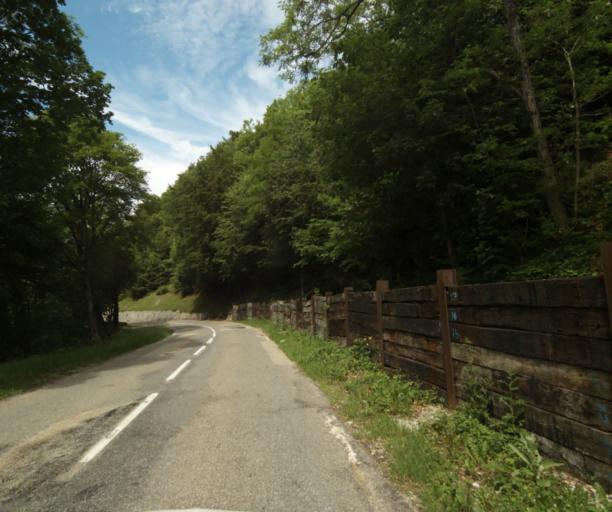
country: FR
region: Rhone-Alpes
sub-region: Departement de la Haute-Savoie
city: Perrignier
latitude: 46.2862
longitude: 6.4608
